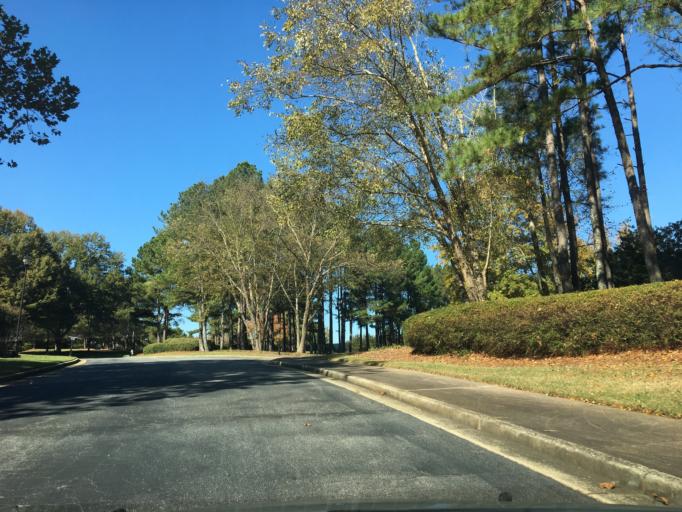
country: US
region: Georgia
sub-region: Fulton County
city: Johns Creek
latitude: 34.0297
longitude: -84.1836
